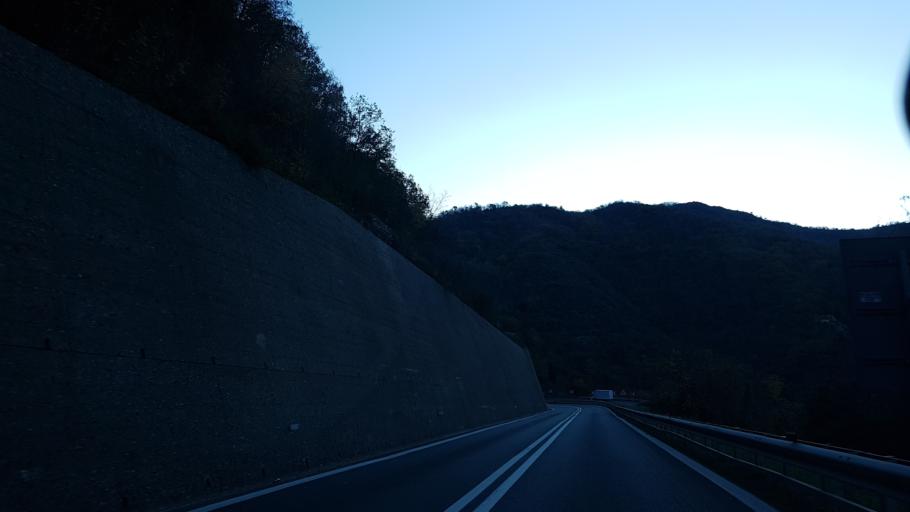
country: IT
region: Liguria
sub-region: Provincia di Genova
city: Avegno
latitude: 44.3776
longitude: 9.1473
